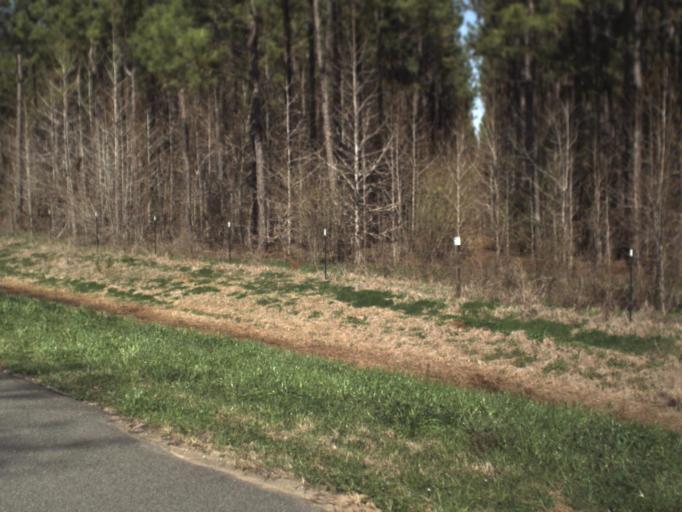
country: US
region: Florida
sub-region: Jackson County
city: Marianna
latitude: 30.8249
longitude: -85.3288
